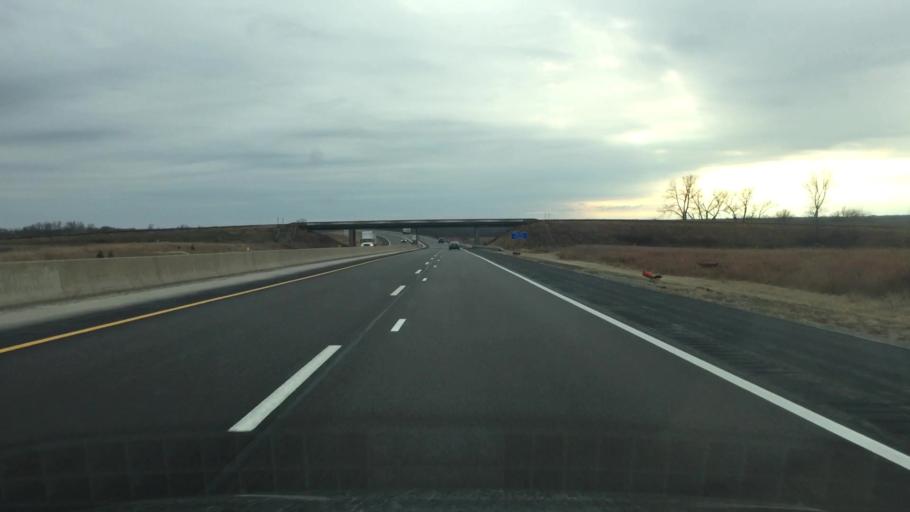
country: US
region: Kansas
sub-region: Osage County
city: Osage City
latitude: 38.6368
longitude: -96.0402
